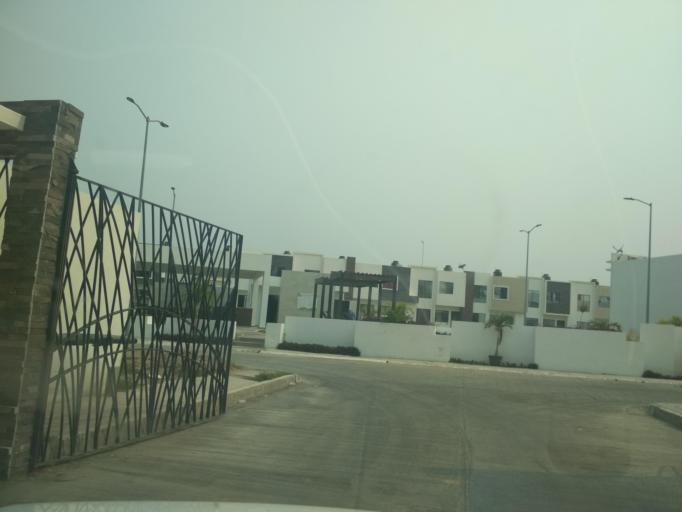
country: MX
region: Veracruz
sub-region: Veracruz
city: Las Amapolas
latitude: 19.1410
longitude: -96.2215
